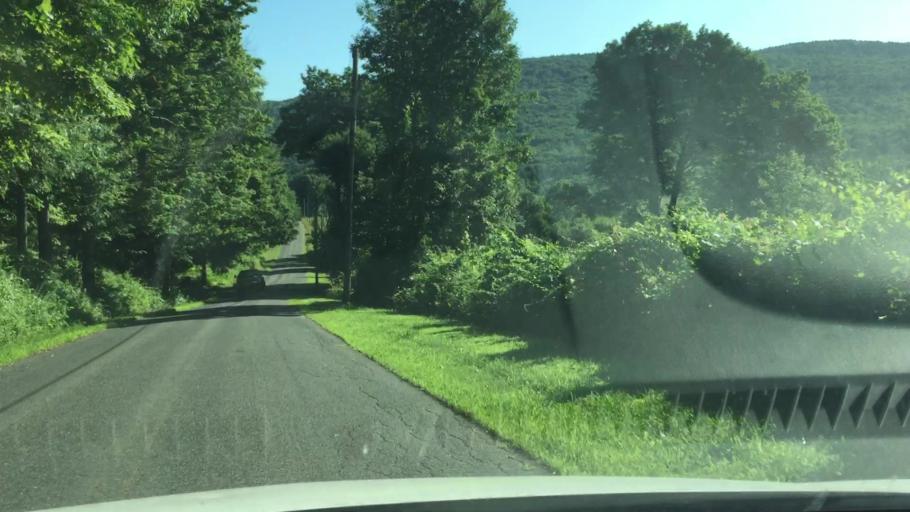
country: US
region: Massachusetts
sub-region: Berkshire County
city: Lee
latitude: 42.2396
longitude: -73.2083
